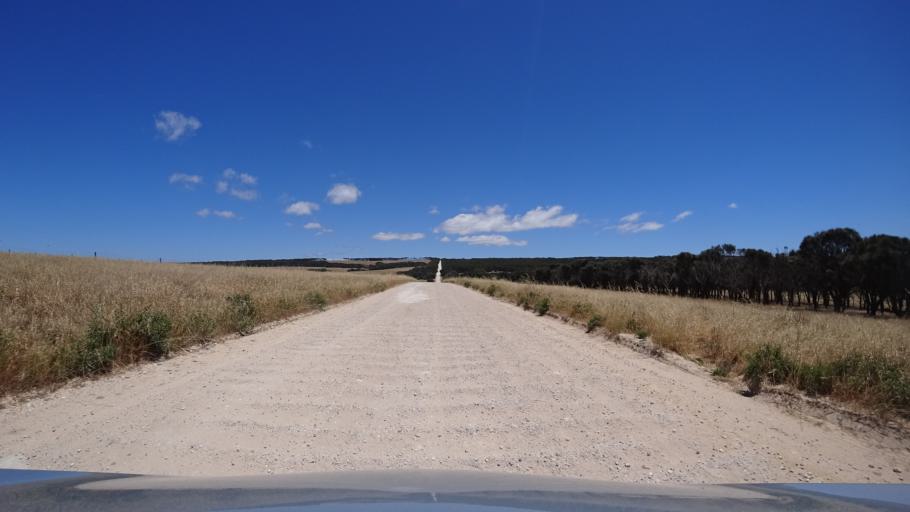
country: AU
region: South Australia
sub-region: Yankalilla
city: Normanville
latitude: -35.8401
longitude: 138.1235
